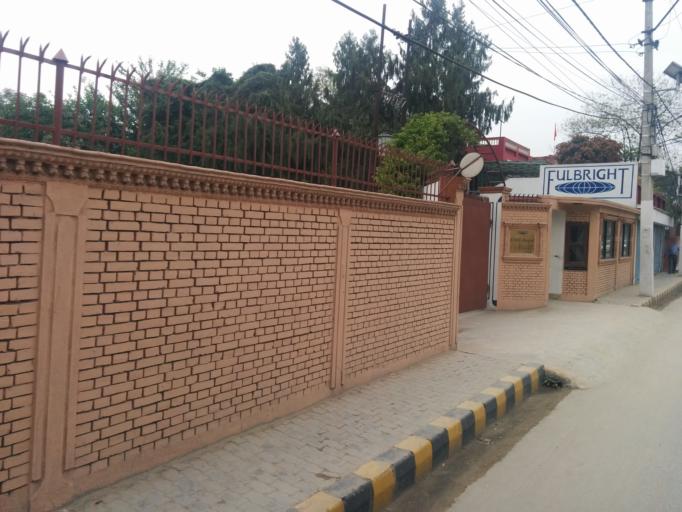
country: NP
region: Central Region
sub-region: Bagmati Zone
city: Kathmandu
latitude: 27.7094
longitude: 85.3294
